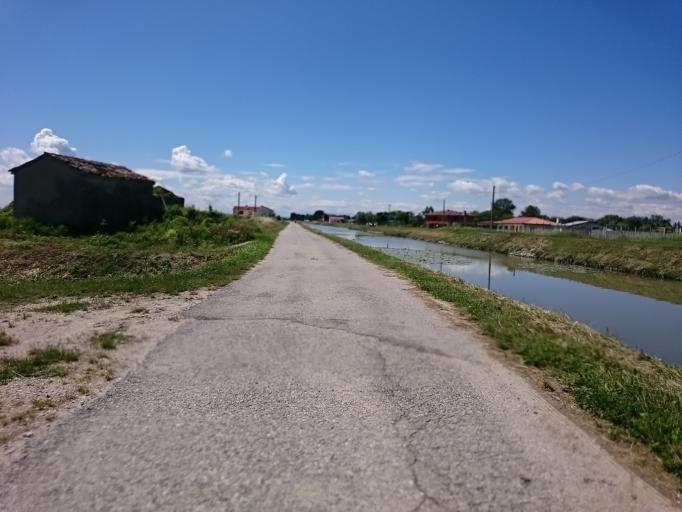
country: IT
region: Veneto
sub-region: Provincia di Padova
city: Codevigo
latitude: 45.2429
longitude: 12.1212
